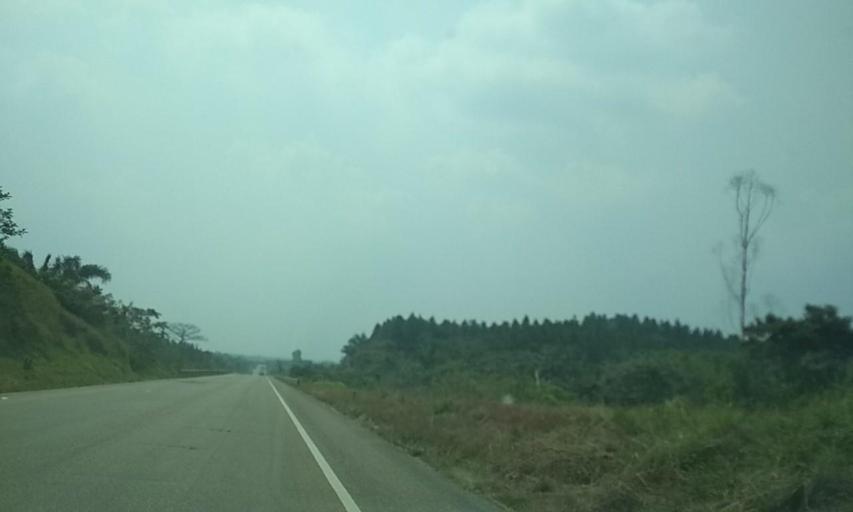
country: MX
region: Tabasco
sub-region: Huimanguillo
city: Francisco Rueda
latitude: 17.7527
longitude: -93.9980
